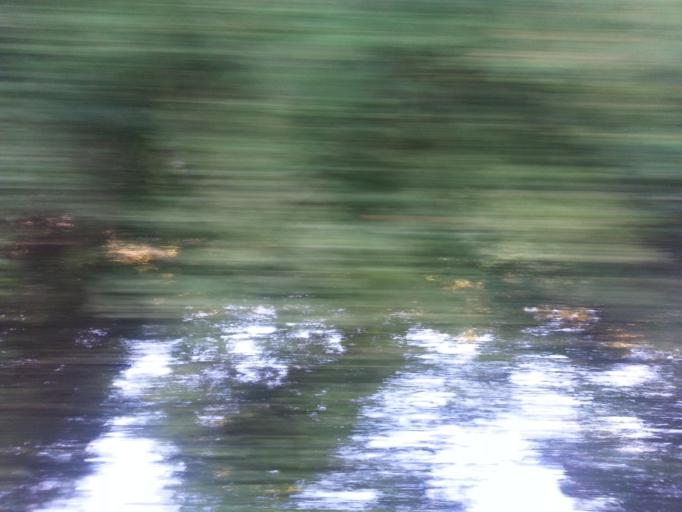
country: US
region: Tennessee
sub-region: Union County
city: Luttrell
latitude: 36.2212
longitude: -83.7304
